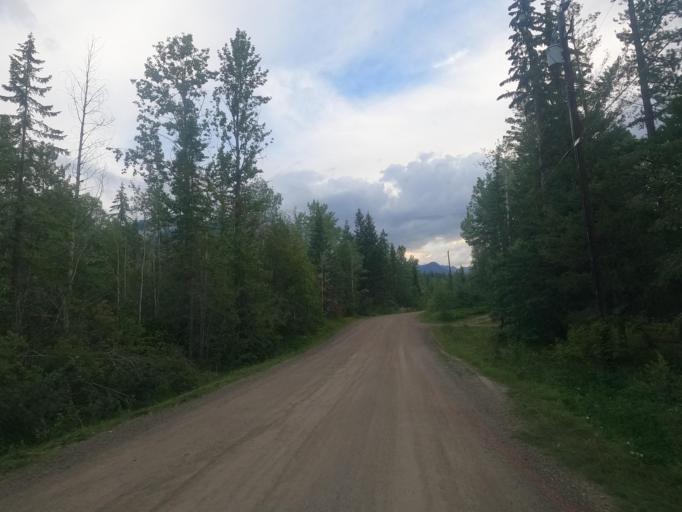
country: CA
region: British Columbia
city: Golden
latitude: 51.4478
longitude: -117.0069
